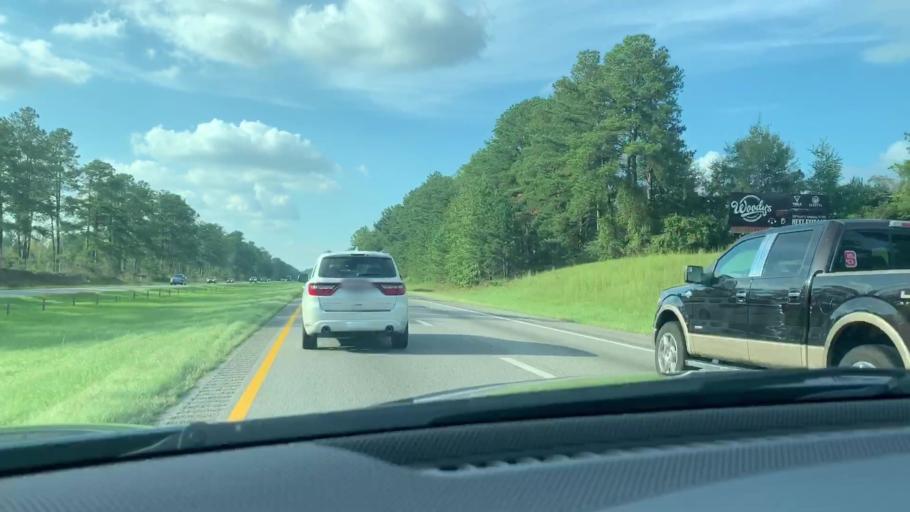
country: US
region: South Carolina
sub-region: Orangeburg County
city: Brookdale
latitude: 33.5403
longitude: -80.8087
